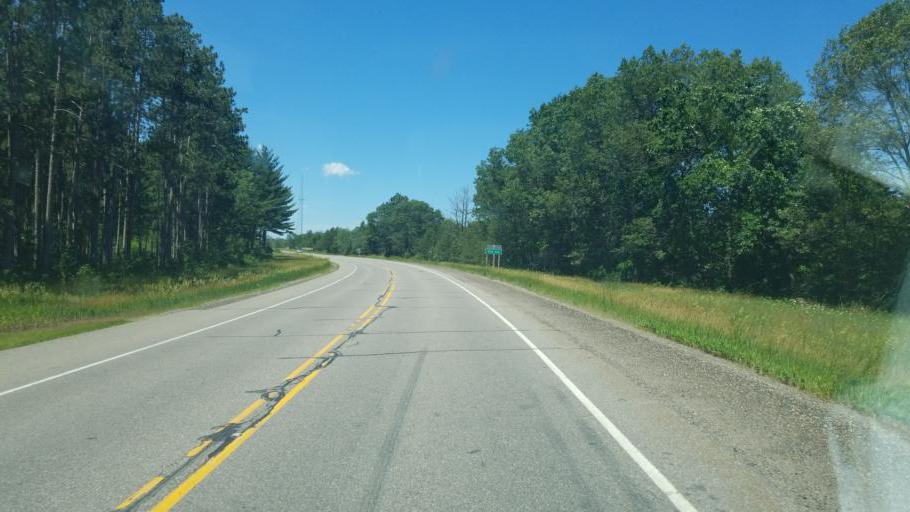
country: US
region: Wisconsin
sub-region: Adams County
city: Friendship
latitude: 44.0467
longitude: -89.9727
